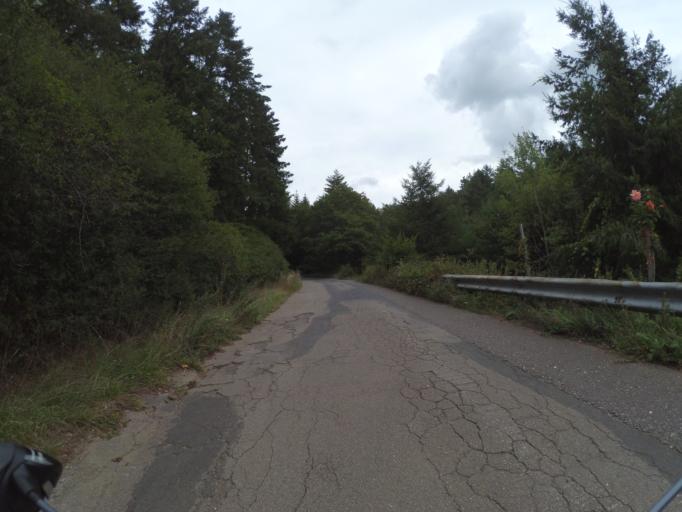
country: DE
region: Rheinland-Pfalz
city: Rivenich
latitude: 49.8661
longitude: 6.8652
